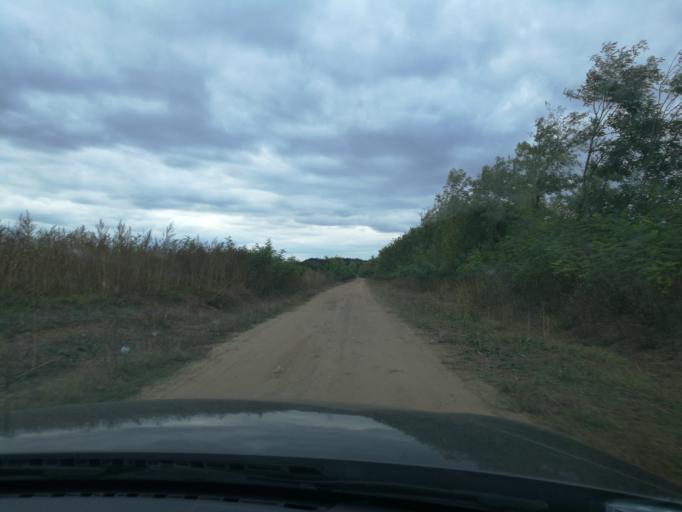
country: HU
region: Szabolcs-Szatmar-Bereg
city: Nyirpazony
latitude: 47.9910
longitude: 21.7885
